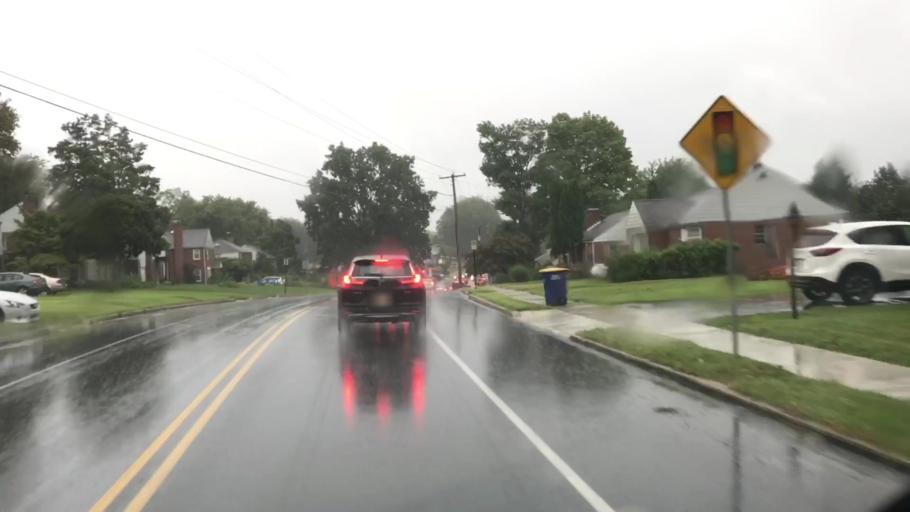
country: US
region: Pennsylvania
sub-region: Cumberland County
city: Lower Allen
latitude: 40.2309
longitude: -76.9083
